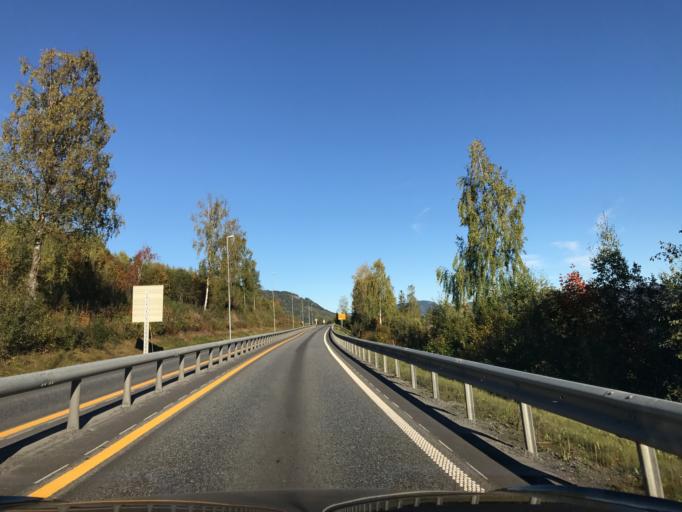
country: NO
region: Oppland
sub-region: Lillehammer
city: Lillehammer
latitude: 61.0518
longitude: 10.4350
